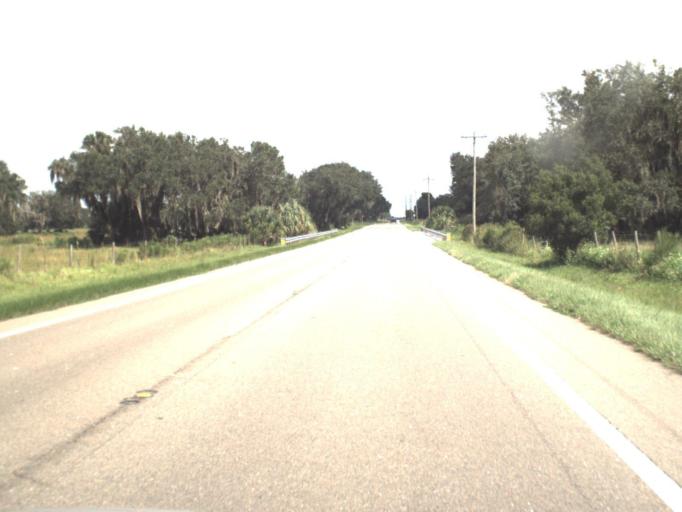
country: US
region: Florida
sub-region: Hardee County
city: Zolfo Springs
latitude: 27.4823
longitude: -81.8816
